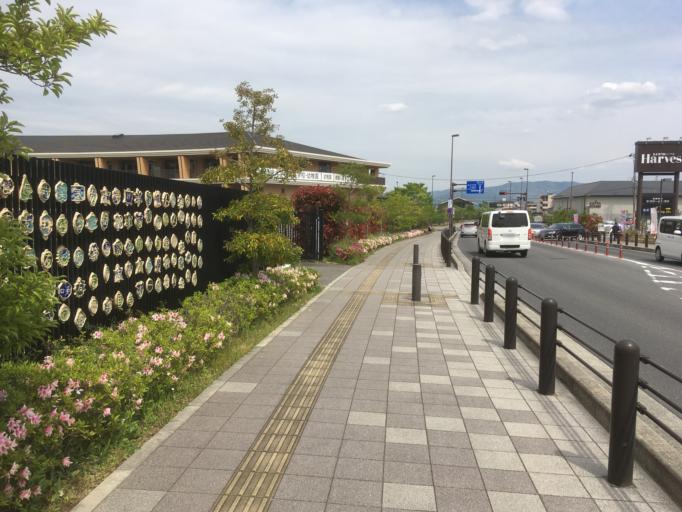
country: JP
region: Nara
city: Nara-shi
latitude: 34.6988
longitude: 135.7614
